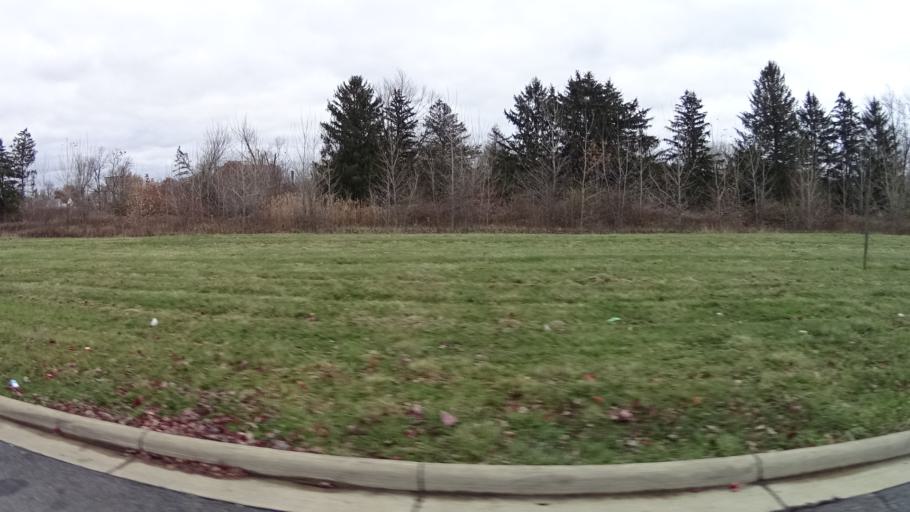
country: US
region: Ohio
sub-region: Lorain County
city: Elyria
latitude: 41.3633
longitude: -82.1150
